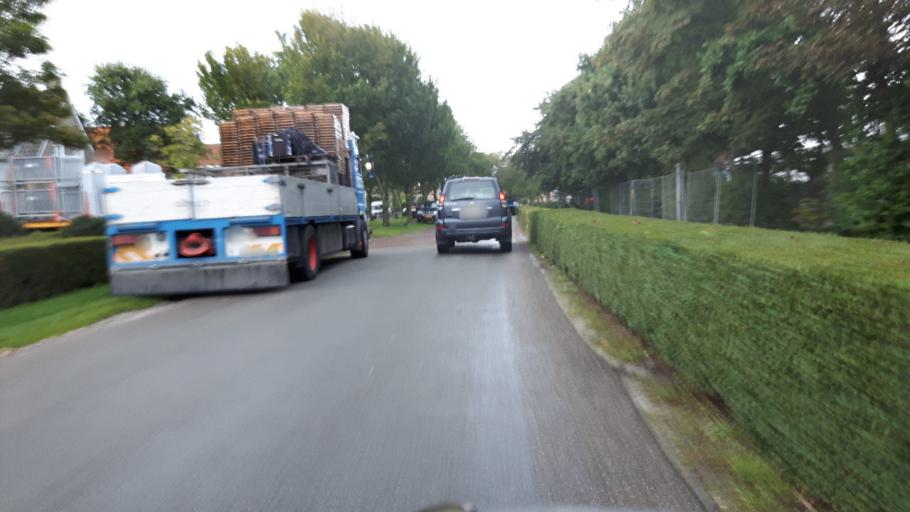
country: NL
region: Friesland
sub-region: Gemeente Ameland
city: Nes
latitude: 53.4489
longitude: 5.7722
